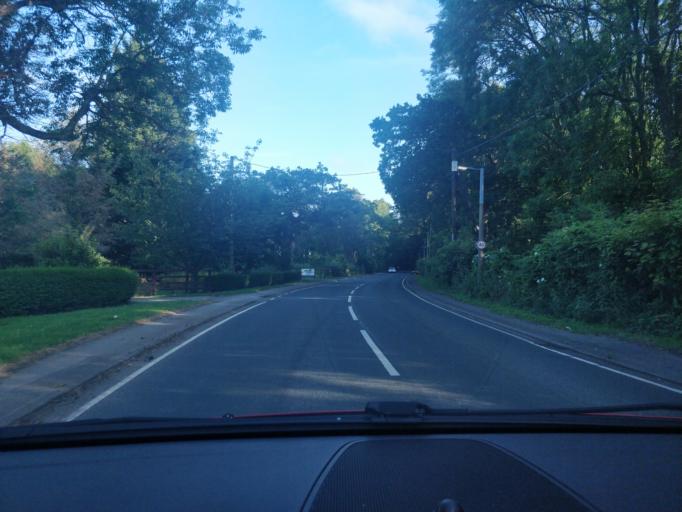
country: GB
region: England
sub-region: Lancashire
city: Banks
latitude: 53.6581
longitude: -2.8790
